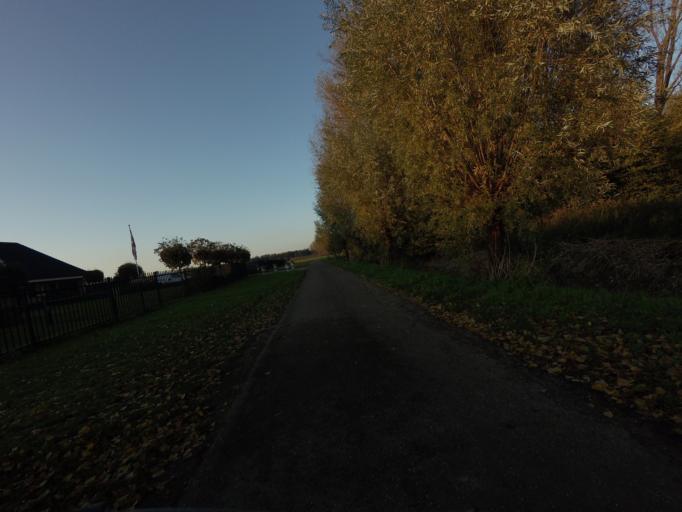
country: NL
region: North Brabant
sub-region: Gemeente Woudrichem
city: Woudrichem
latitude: 51.7906
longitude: 5.0208
